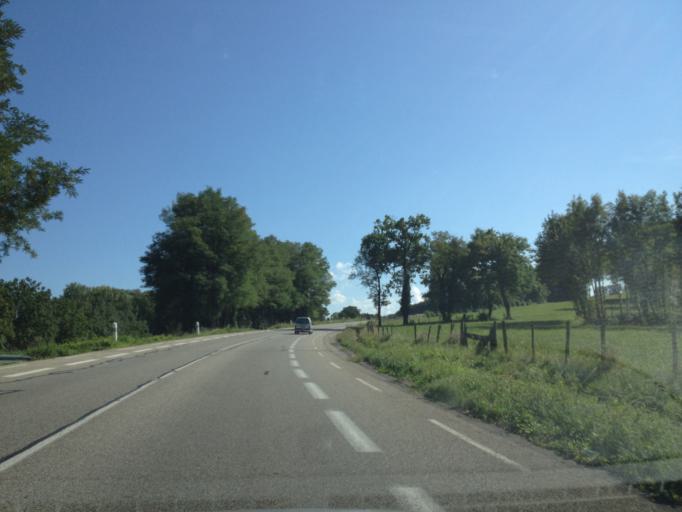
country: FR
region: Rhone-Alpes
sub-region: Departement de la Savoie
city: Sonnaz
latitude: 45.6294
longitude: 5.9143
